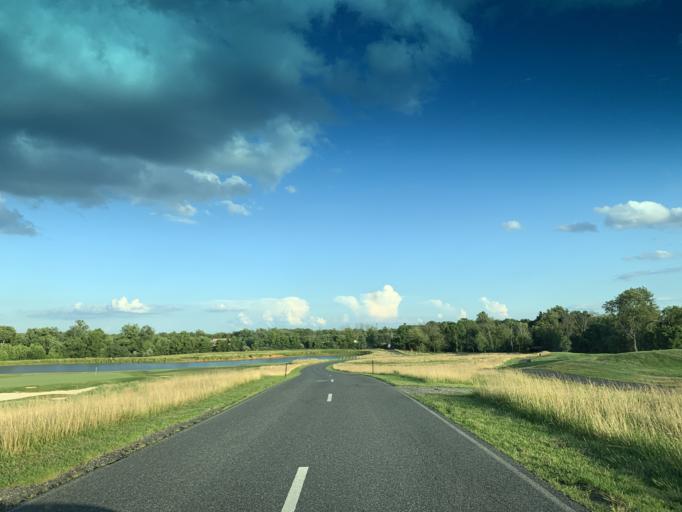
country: US
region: Maryland
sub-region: Harford County
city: Havre de Grace
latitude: 39.5351
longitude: -76.1283
